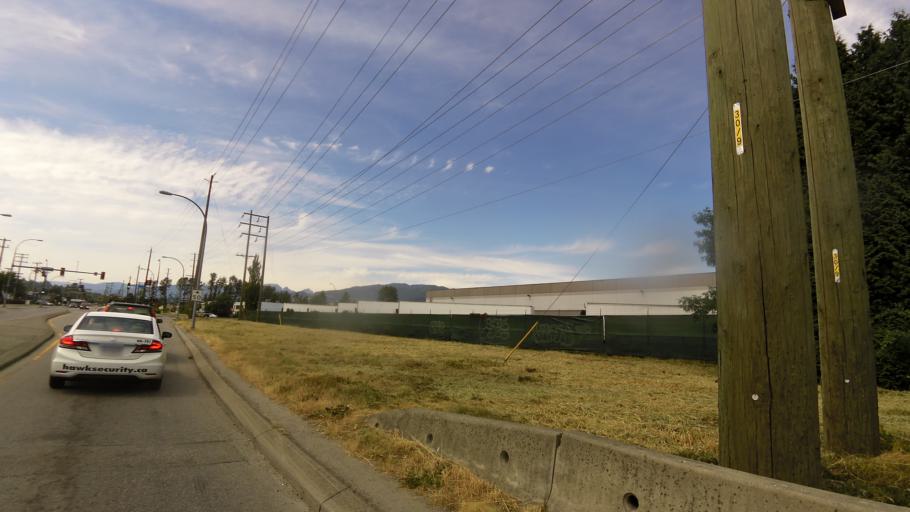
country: CA
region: British Columbia
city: Coquitlam
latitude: 49.2523
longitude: -122.7610
